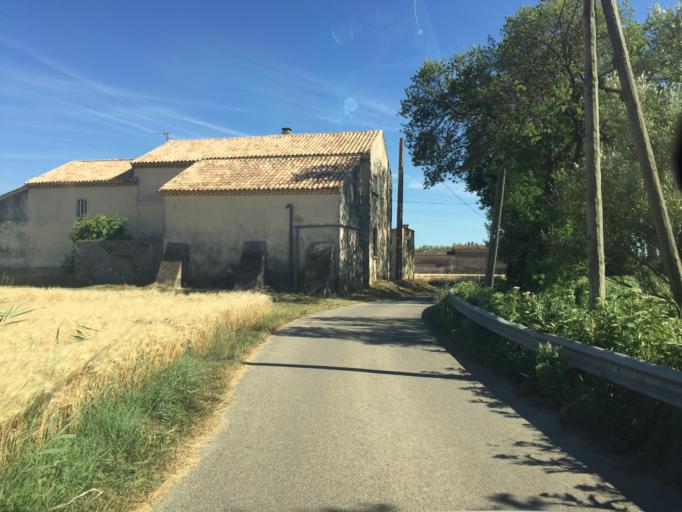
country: FR
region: Provence-Alpes-Cote d'Azur
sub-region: Departement du Vaucluse
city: Caderousse
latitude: 44.1042
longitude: 4.7424
